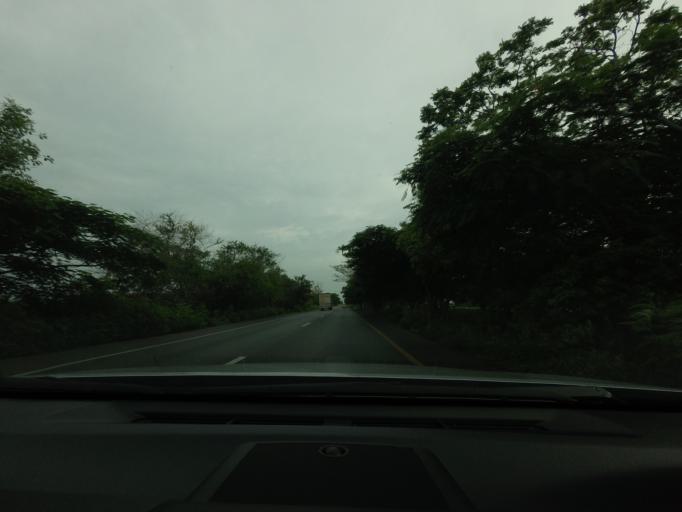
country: TH
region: Phetchaburi
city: Cha-am
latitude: 12.7584
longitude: 99.9331
